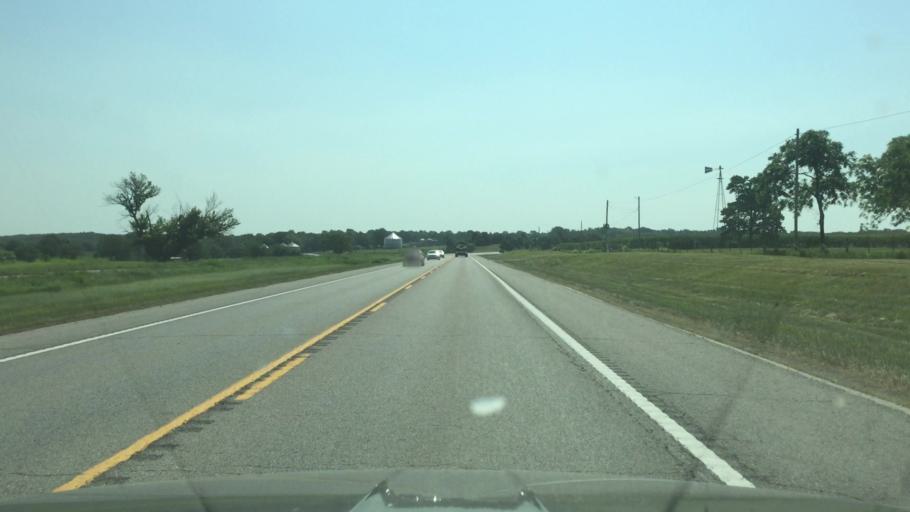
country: US
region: Missouri
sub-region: Pettis County
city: Sedalia
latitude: 38.6915
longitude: -93.0581
